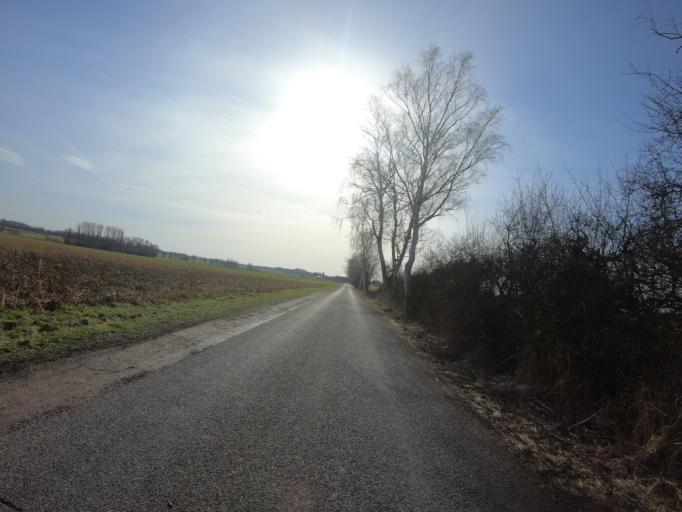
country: DE
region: Lower Saxony
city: Isenbuttel
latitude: 52.4160
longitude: 10.5646
